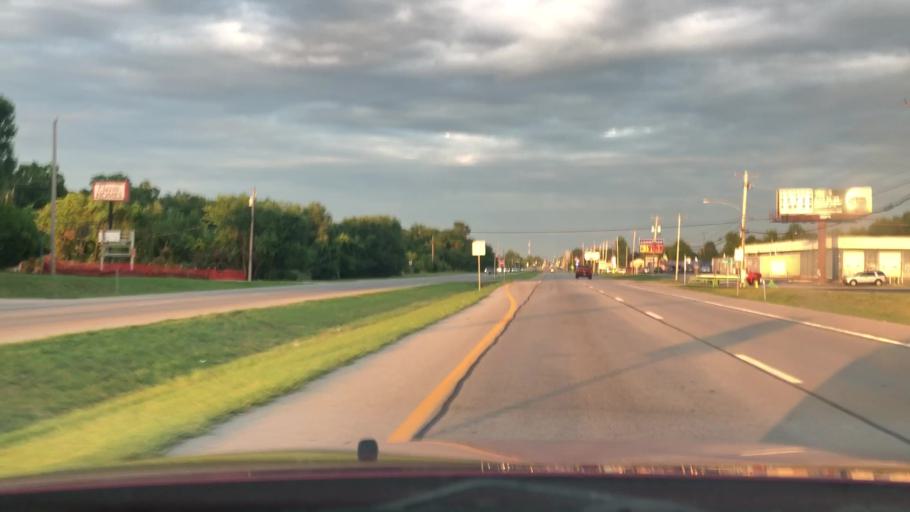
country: US
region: Missouri
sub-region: Greene County
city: Springfield
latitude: 37.1828
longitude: -93.3371
